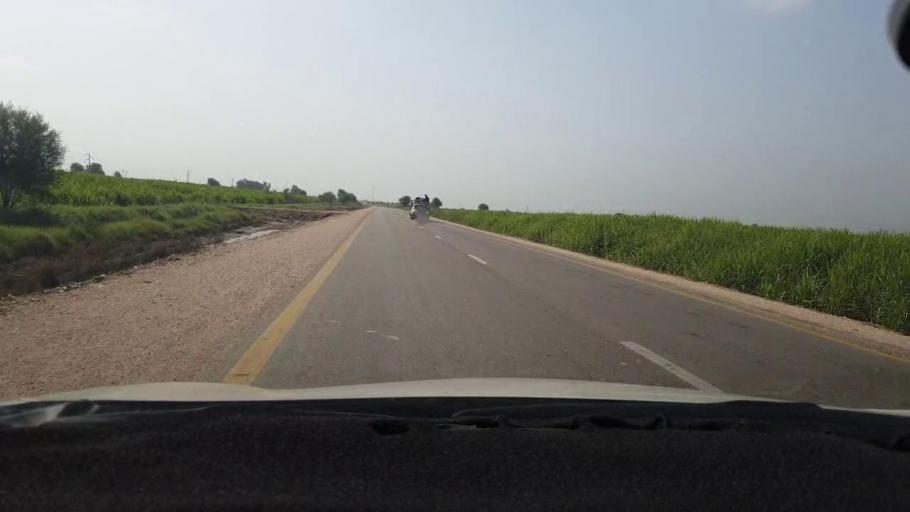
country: PK
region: Sindh
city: Jhol
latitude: 25.8463
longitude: 69.0613
